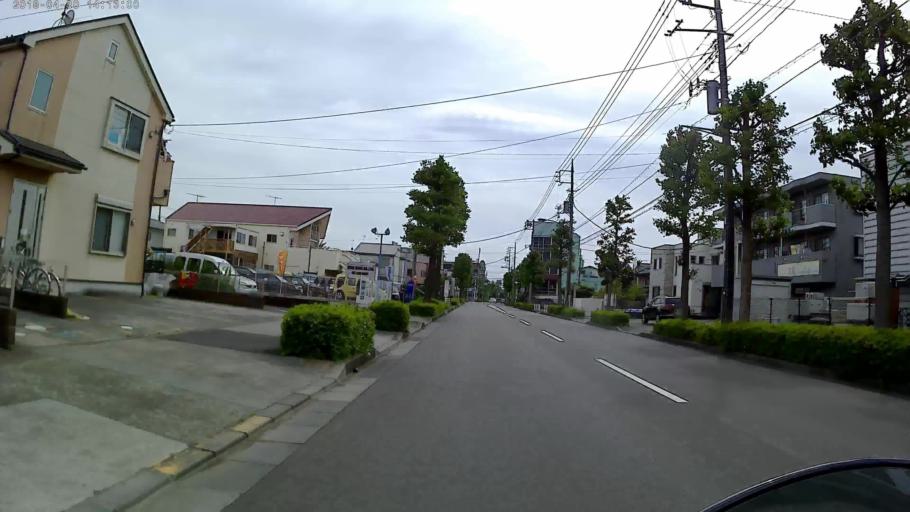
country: JP
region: Tokyo
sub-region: Machida-shi
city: Machida
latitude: 35.5733
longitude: 139.4157
